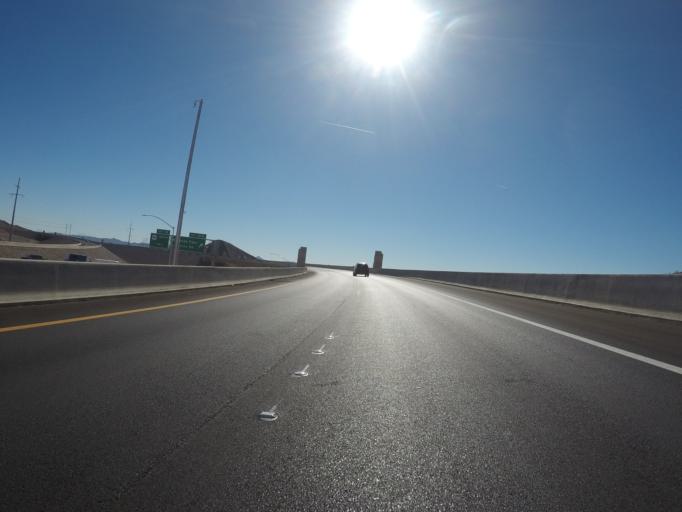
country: US
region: Nevada
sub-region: Clark County
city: Boulder City
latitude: 35.9708
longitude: -114.9141
